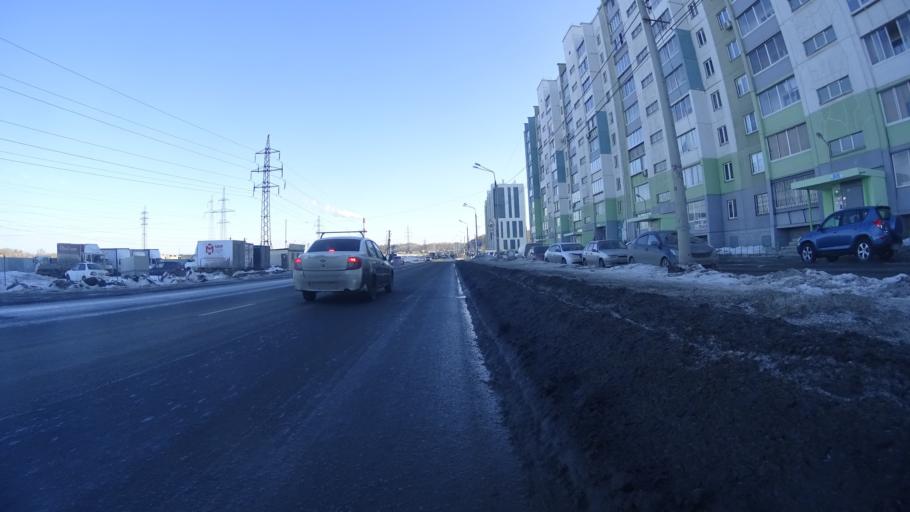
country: RU
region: Chelyabinsk
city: Roshchino
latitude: 55.2156
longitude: 61.3033
